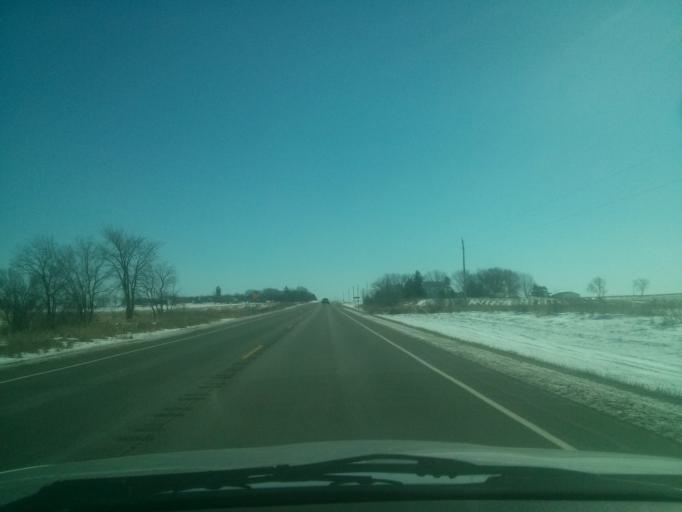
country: US
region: Wisconsin
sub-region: Polk County
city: Clear Lake
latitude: 45.1363
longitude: -92.3269
